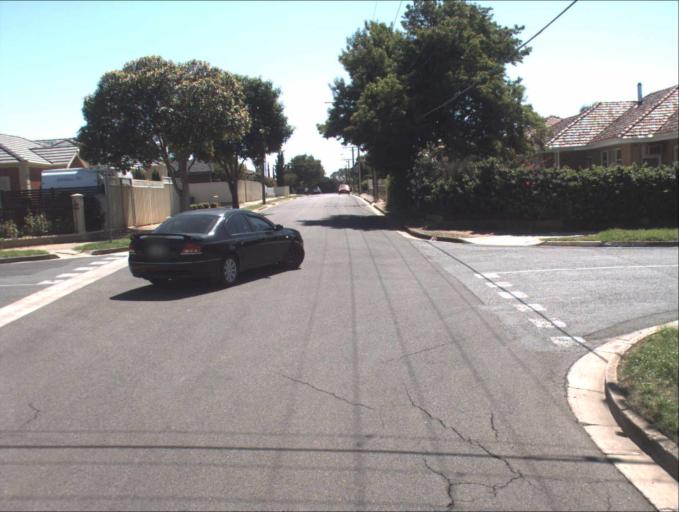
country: AU
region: South Australia
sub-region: Port Adelaide Enfield
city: Klemzig
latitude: -34.8809
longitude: 138.6282
